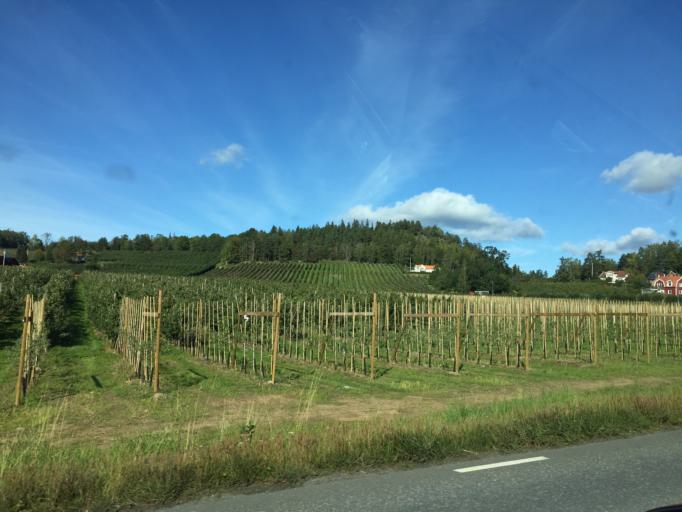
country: SE
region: Joenkoeping
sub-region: Jonkopings Kommun
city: Kaxholmen
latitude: 57.8421
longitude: 14.2839
